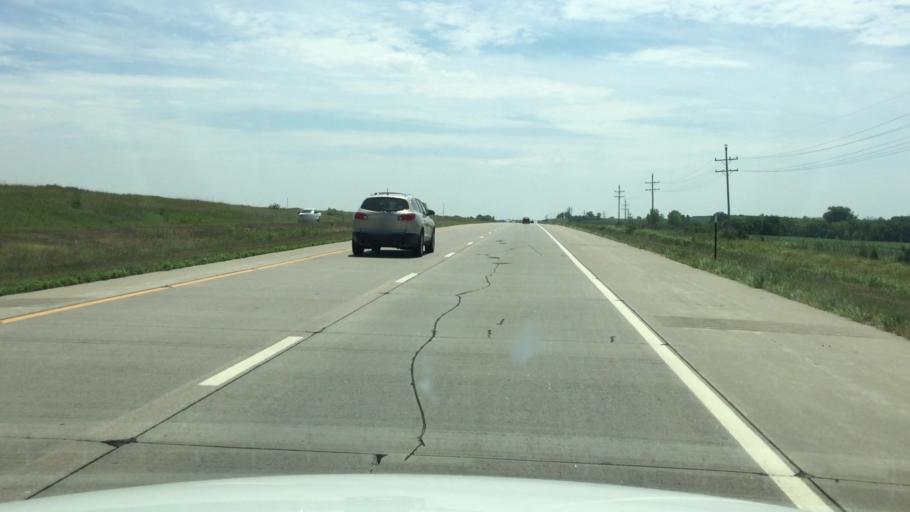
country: US
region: Kansas
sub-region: Shawnee County
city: Silver Lake
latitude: 39.2375
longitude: -95.7197
